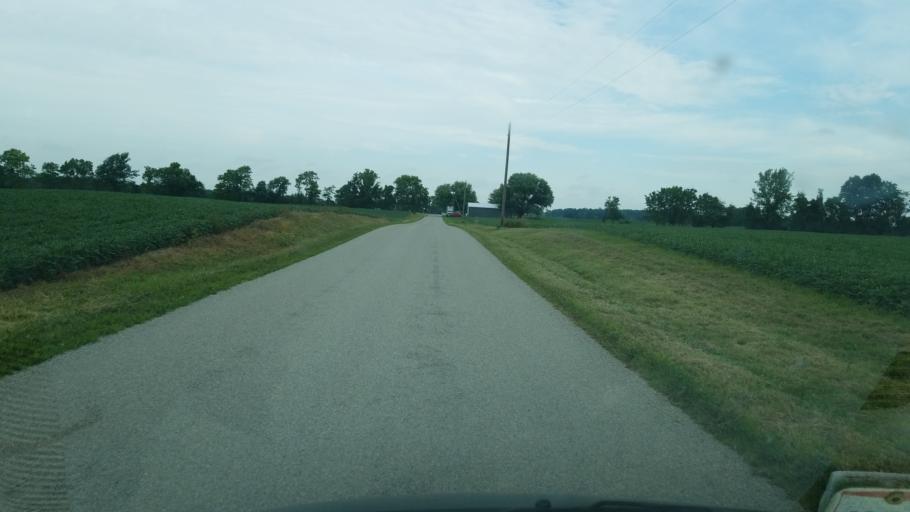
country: US
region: Ohio
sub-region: Seneca County
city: Tiffin
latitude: 41.0280
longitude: -83.0546
